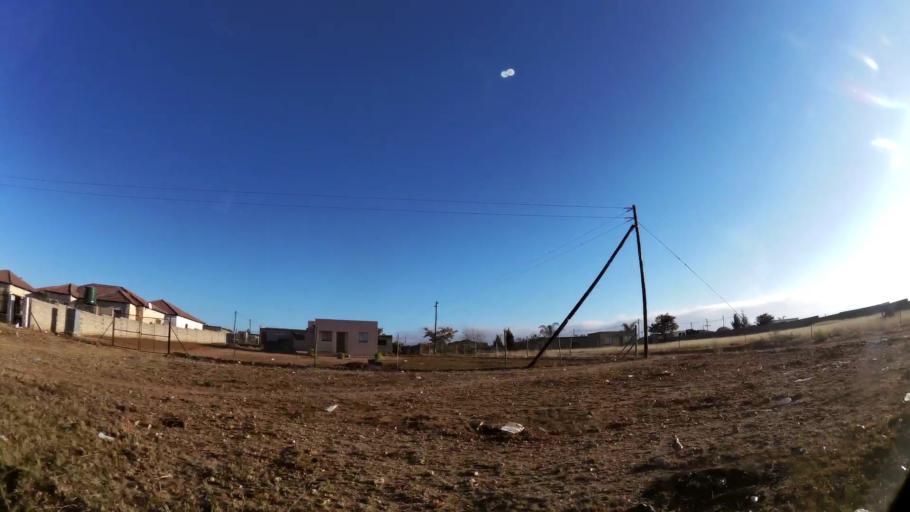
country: ZA
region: Limpopo
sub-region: Capricorn District Municipality
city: Polokwane
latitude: -23.8408
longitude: 29.3650
